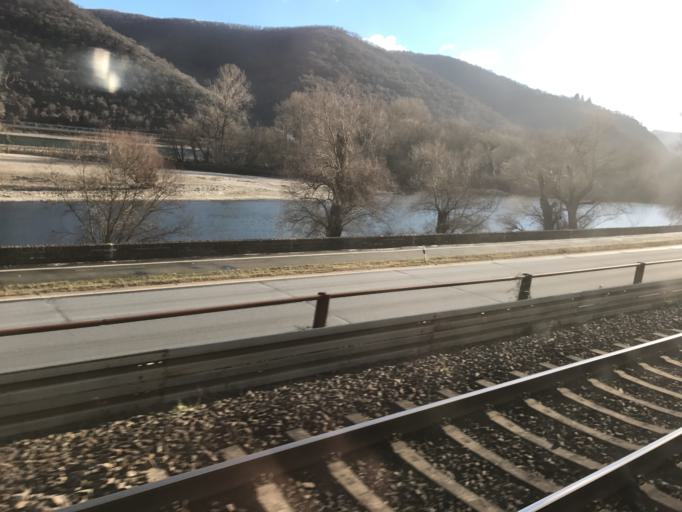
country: DE
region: Rheinland-Pfalz
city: Bacharach
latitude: 50.0698
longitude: 7.7702
